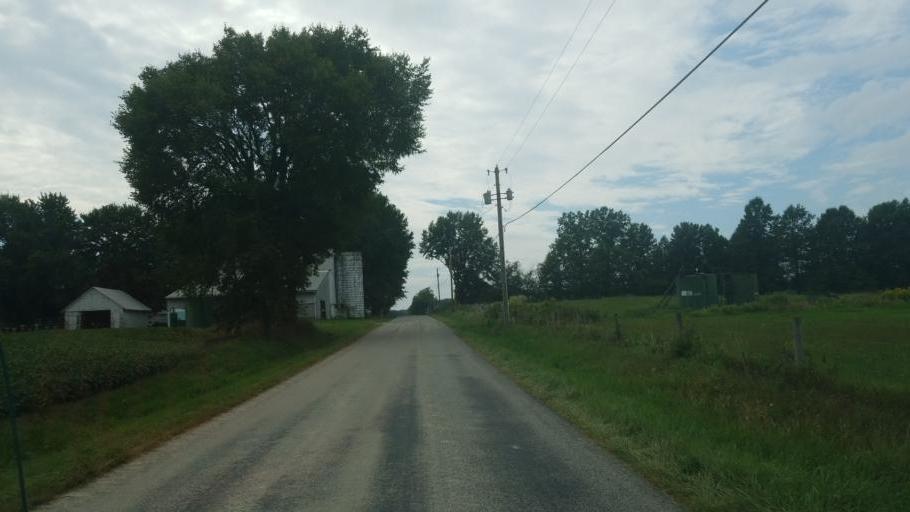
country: US
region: Ohio
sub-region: Wayne County
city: Smithville
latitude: 40.9082
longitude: -81.9417
